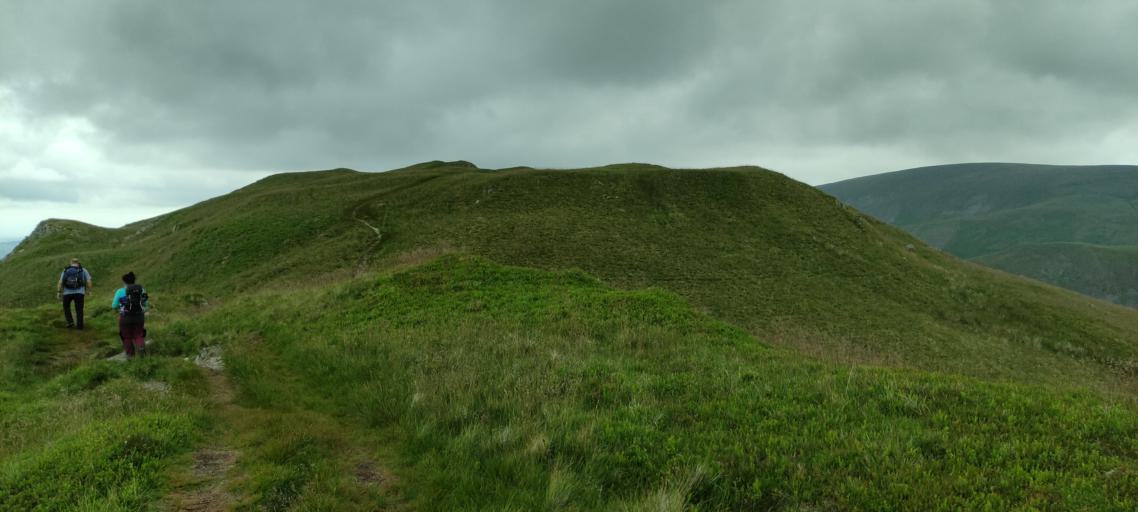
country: GB
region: England
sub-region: Cumbria
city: Ambleside
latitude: 54.5435
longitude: -2.8880
